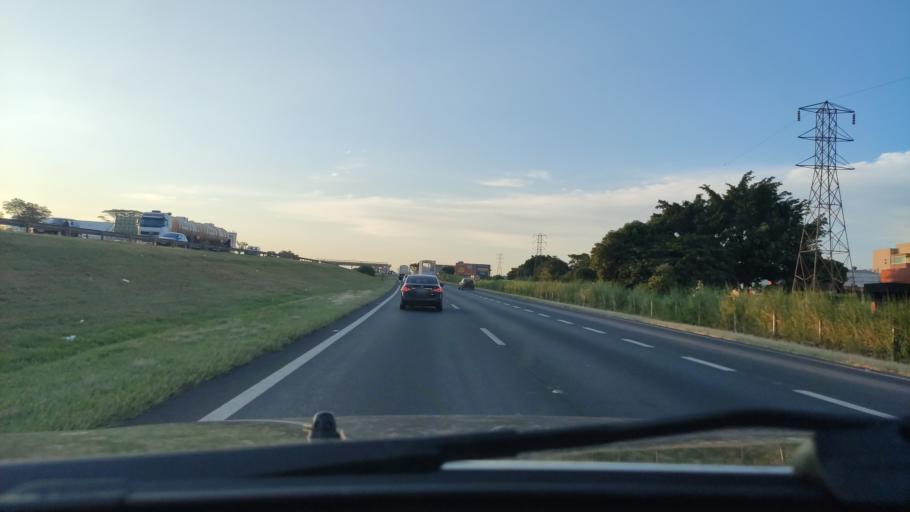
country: BR
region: Sao Paulo
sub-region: Rio Claro
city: Rio Claro
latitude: -22.4174
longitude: -47.5784
